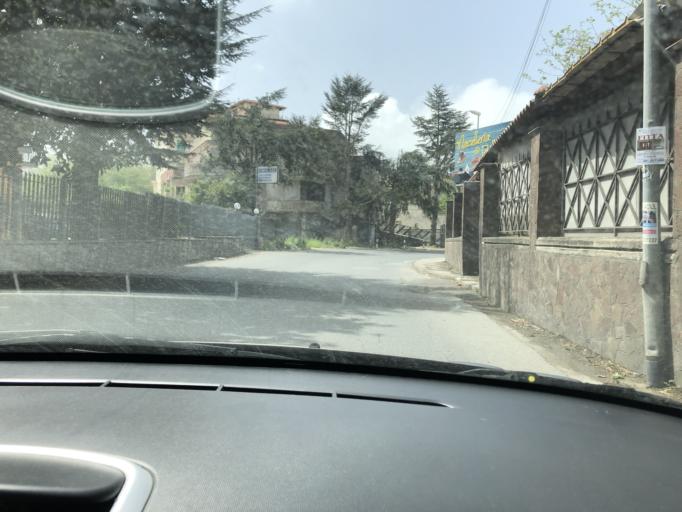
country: IT
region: Campania
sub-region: Provincia di Napoli
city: Torre Caracciolo
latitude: 40.8753
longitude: 14.1835
